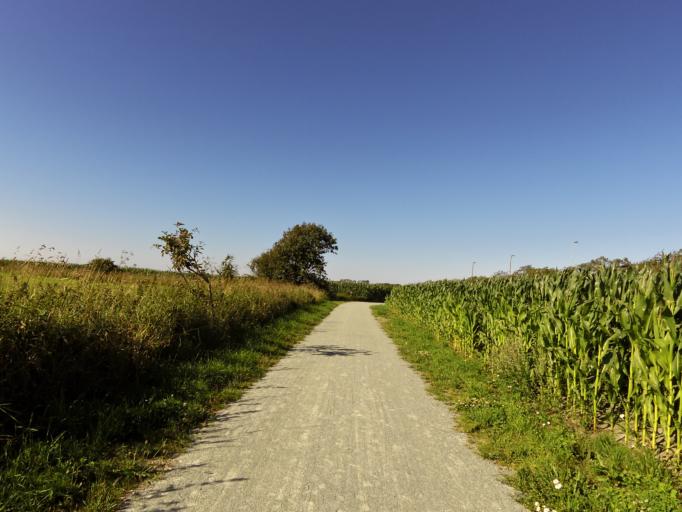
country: DK
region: South Denmark
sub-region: Tonder Kommune
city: Sherrebek
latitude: 55.1553
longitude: 8.7527
